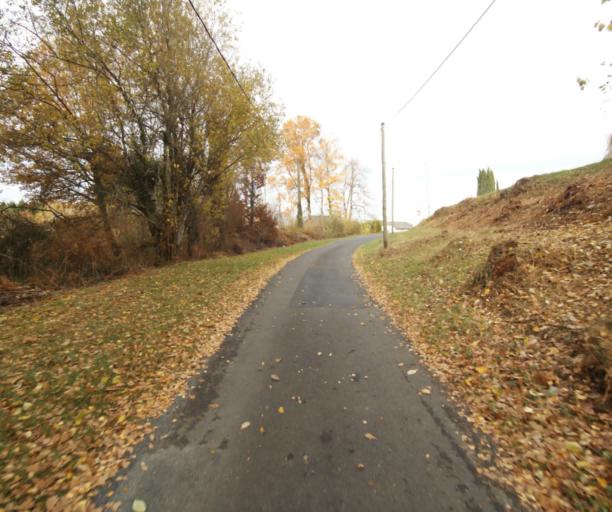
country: FR
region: Limousin
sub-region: Departement de la Correze
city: Sainte-Fortunade
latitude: 45.2025
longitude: 1.7705
